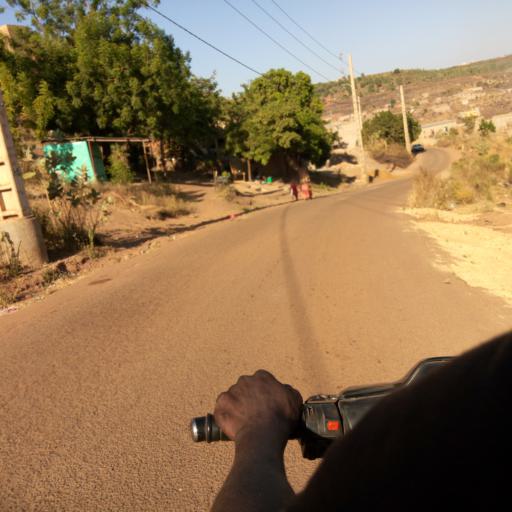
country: ML
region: Bamako
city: Bamako
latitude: 12.6579
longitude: -8.0394
